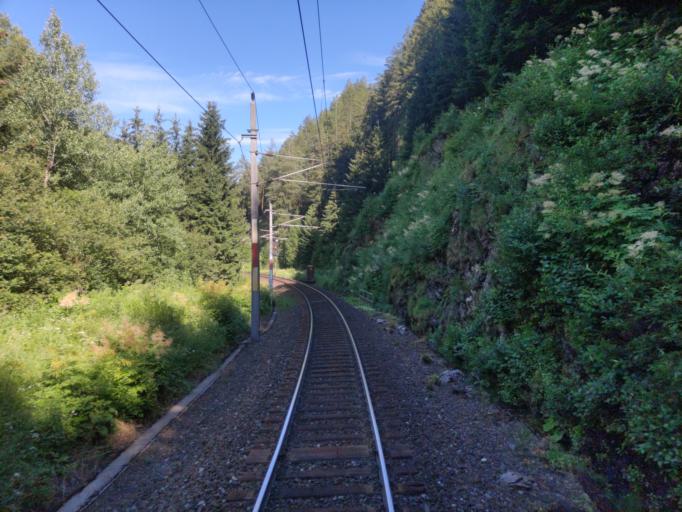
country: AT
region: Tyrol
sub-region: Politischer Bezirk Landeck
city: Strengen
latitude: 47.1273
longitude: 10.4484
